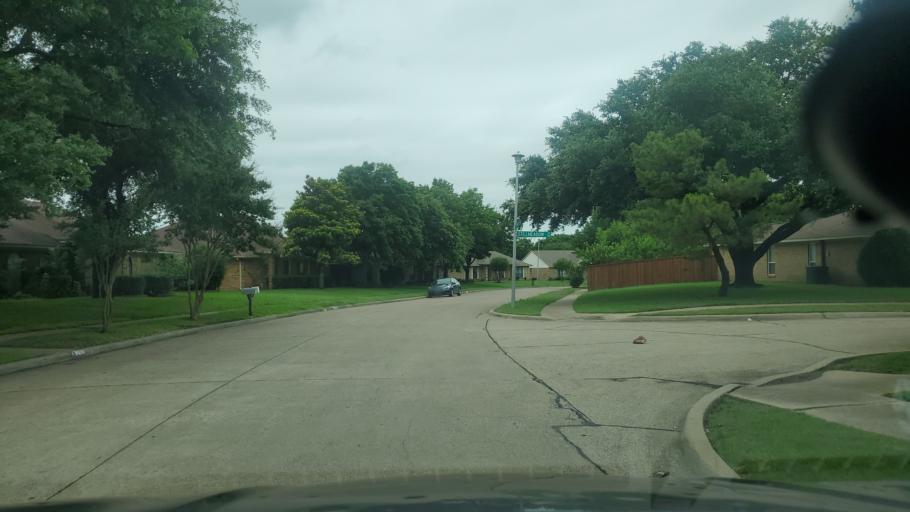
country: US
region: Texas
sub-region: Dallas County
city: Garland
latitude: 32.9396
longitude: -96.6266
